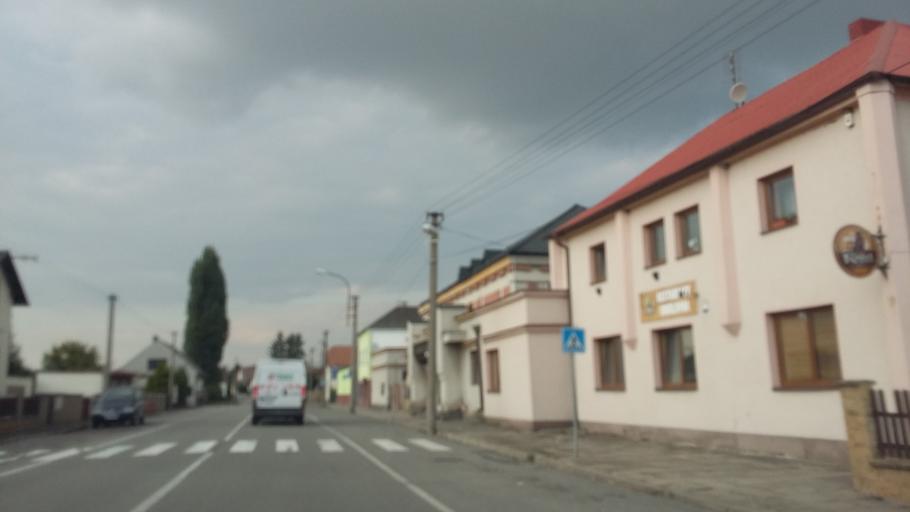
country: CZ
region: Central Bohemia
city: Benatky nad Jizerou
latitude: 50.3274
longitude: 14.8658
